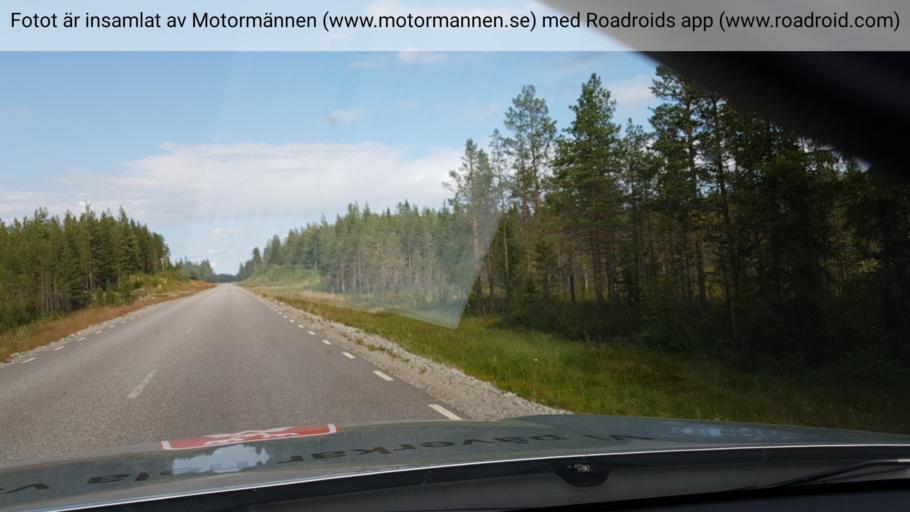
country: SE
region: Vaesterbotten
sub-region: Skelleftea Kommun
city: Boliden
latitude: 65.2989
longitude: 20.2339
